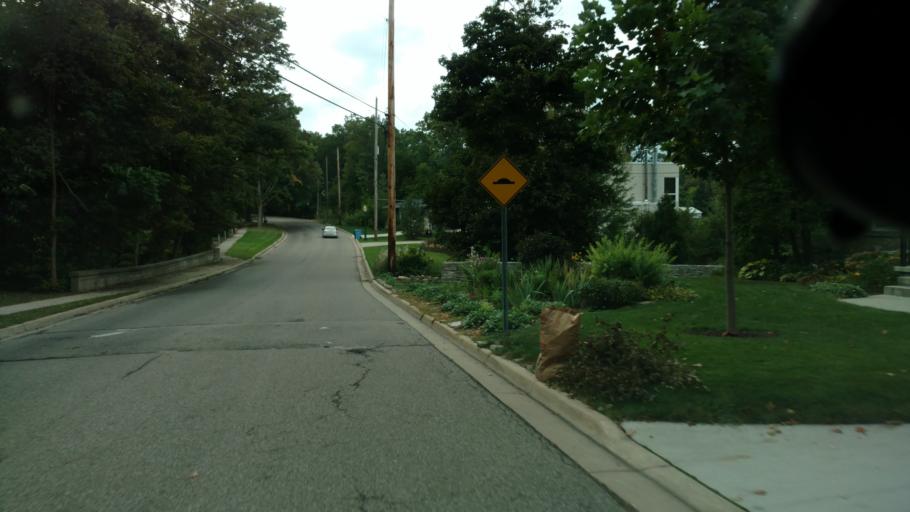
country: US
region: Michigan
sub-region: Ingham County
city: Lansing
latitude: 42.7205
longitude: -84.5814
